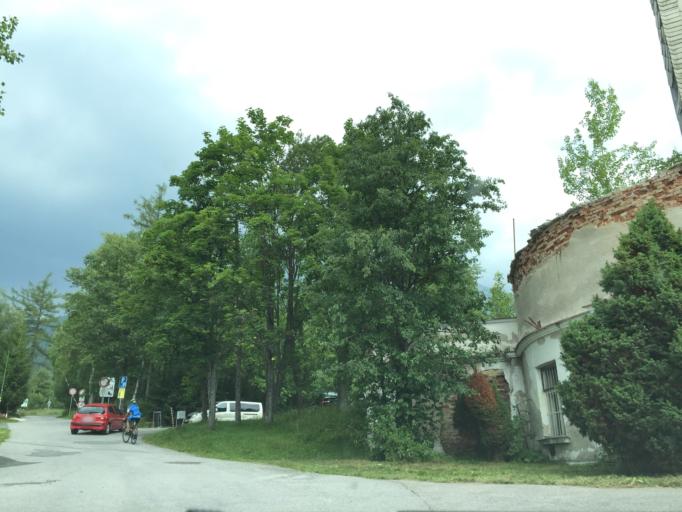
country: SK
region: Presovsky
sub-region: Okres Poprad
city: Vysoke Tatry
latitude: 49.1417
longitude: 20.2225
